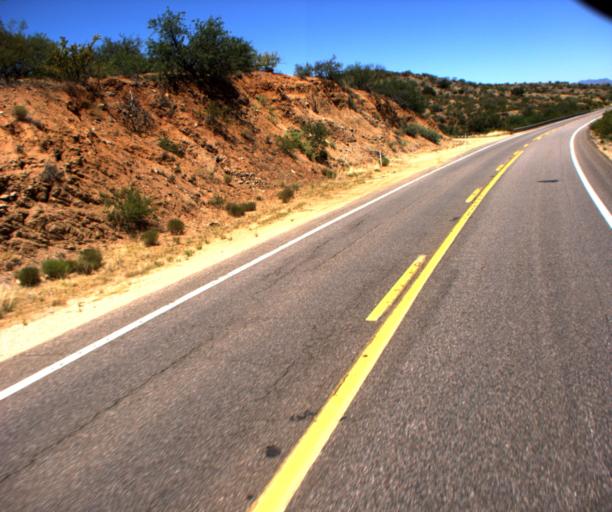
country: US
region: Arizona
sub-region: Gila County
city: Globe
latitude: 33.3164
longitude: -110.7374
